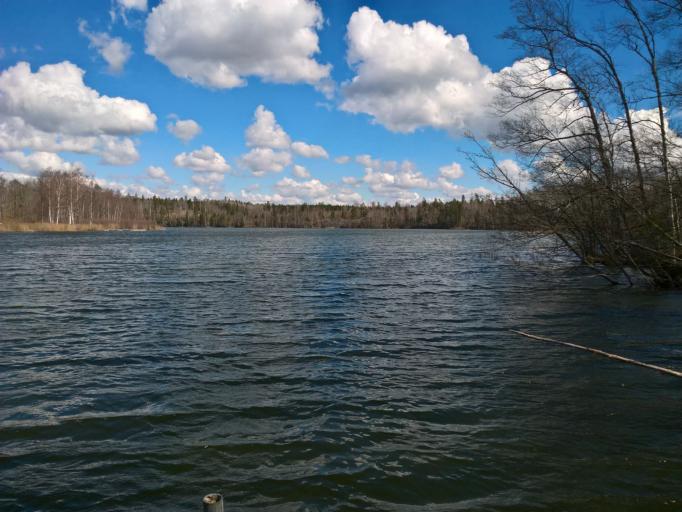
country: SE
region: OEstergoetland
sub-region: Finspangs Kommun
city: Finspang
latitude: 58.7346
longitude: 15.7166
